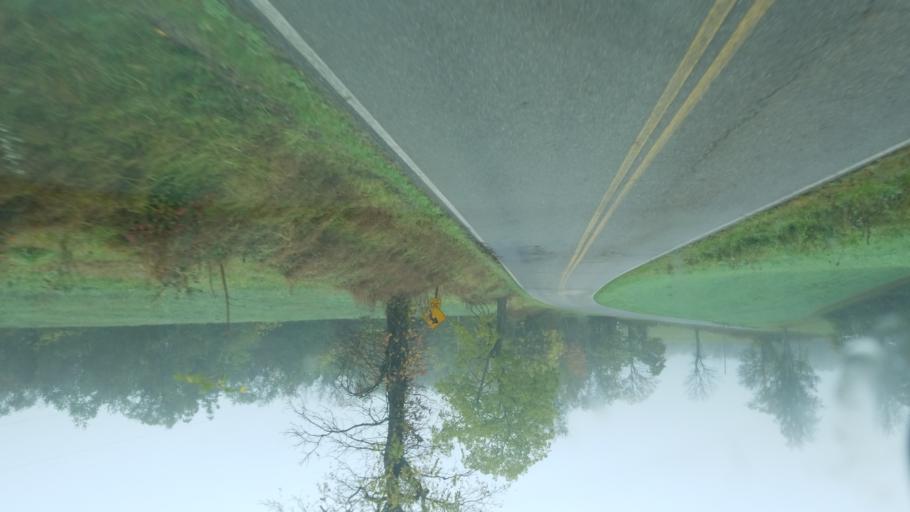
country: US
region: Ohio
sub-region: Harrison County
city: Cadiz
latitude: 40.3792
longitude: -81.1101
